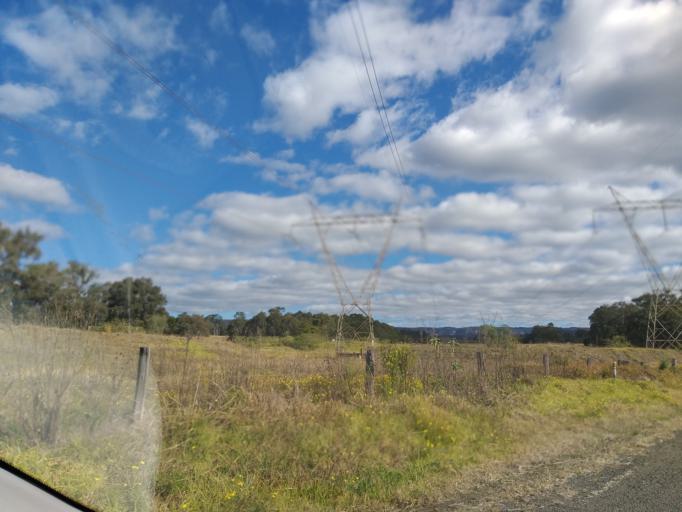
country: AU
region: New South Wales
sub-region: Shellharbour
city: Albion Park Rail
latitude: -34.5380
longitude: 150.7758
